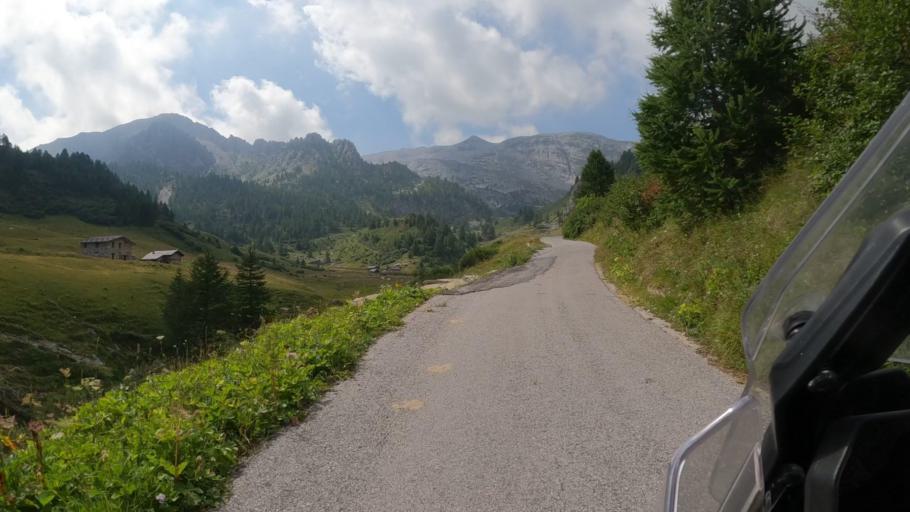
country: IT
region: Piedmont
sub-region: Provincia di Cuneo
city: Marmora
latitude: 44.4042
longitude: 7.1076
